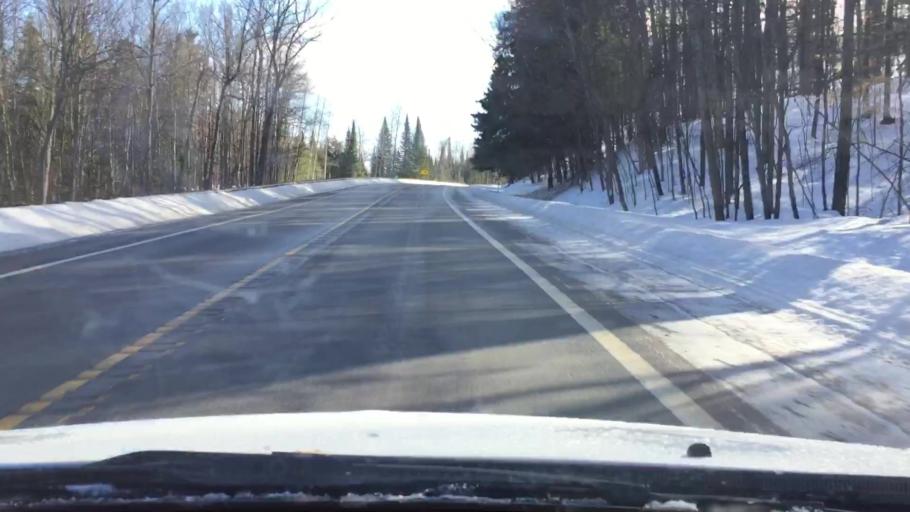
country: US
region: Michigan
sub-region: Antrim County
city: Mancelona
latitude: 44.9991
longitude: -85.0624
